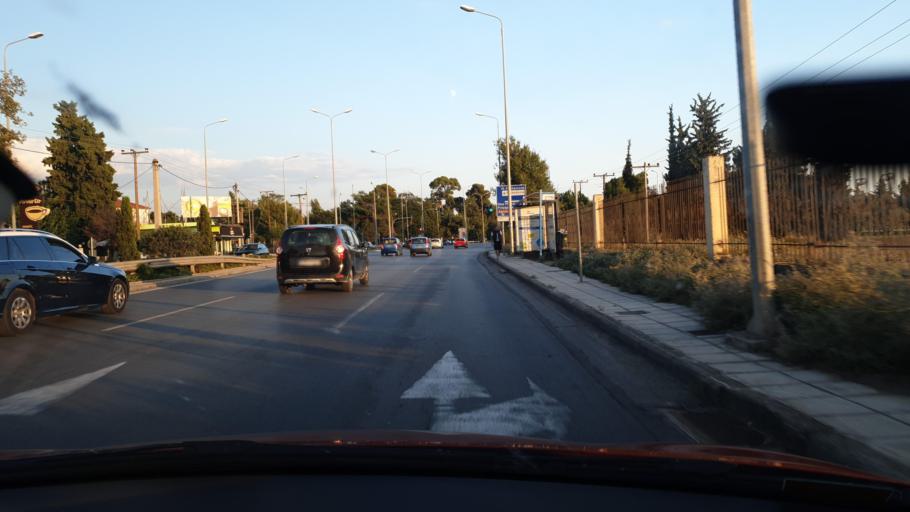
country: GR
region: Central Macedonia
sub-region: Nomos Thessalonikis
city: Thermi
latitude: 40.5400
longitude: 22.9898
